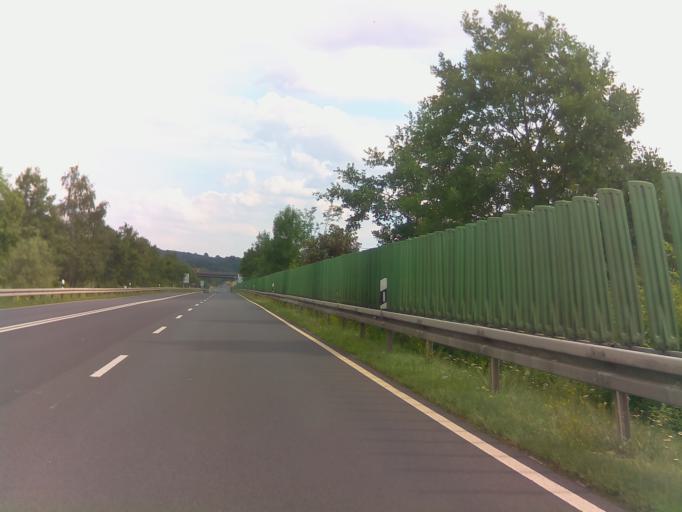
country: DE
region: Hesse
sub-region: Regierungsbezirk Kassel
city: Burghaun
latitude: 50.7270
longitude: 9.7035
